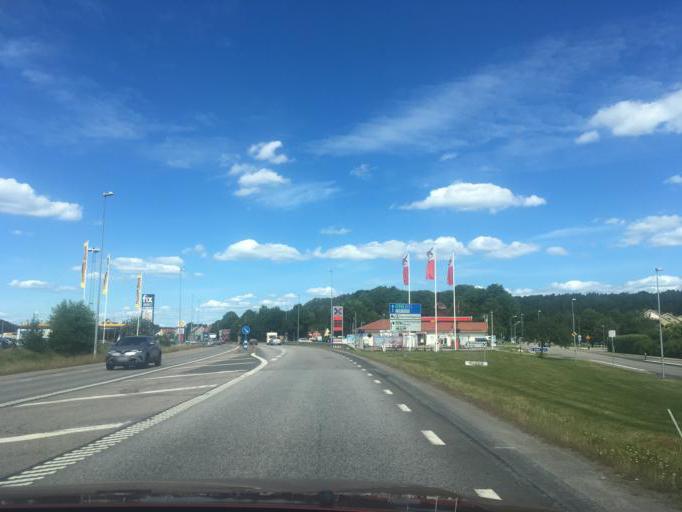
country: SE
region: OEstergoetland
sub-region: Soderkopings Kommun
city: Soederkoeping
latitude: 58.4752
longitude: 16.3365
